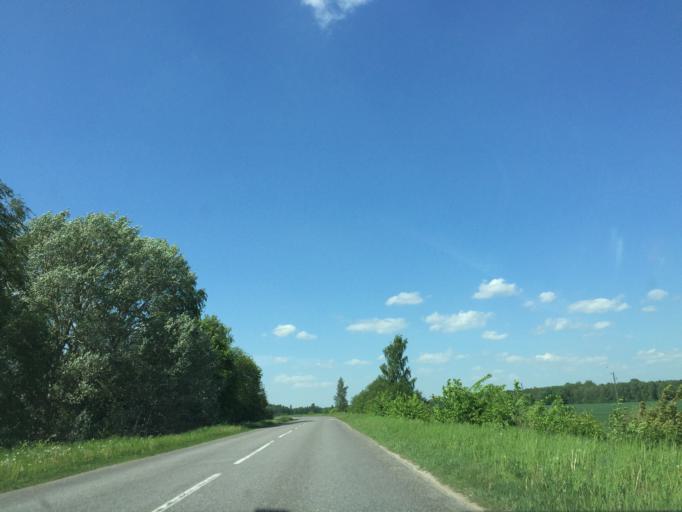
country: LV
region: Rundales
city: Pilsrundale
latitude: 56.5862
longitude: 23.9676
